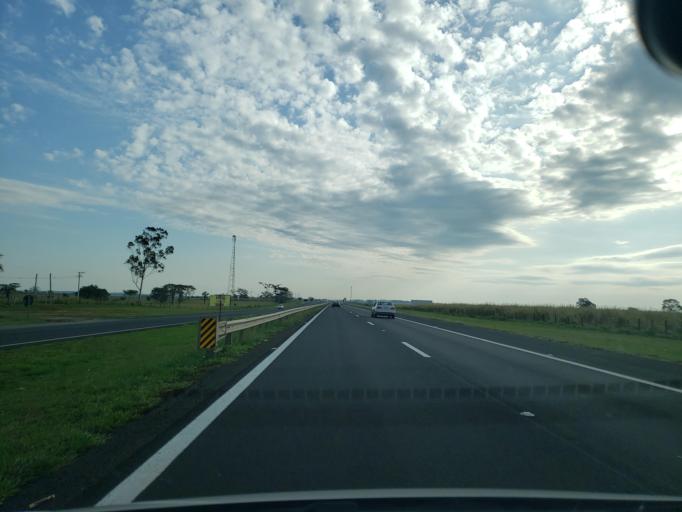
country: BR
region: Sao Paulo
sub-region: Guararapes
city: Guararapes
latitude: -21.2056
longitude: -50.6300
